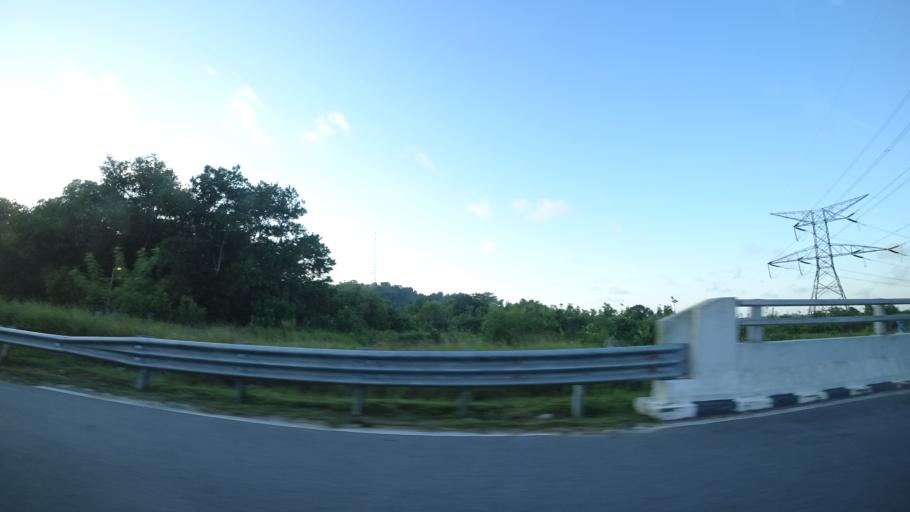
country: BN
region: Tutong
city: Tutong
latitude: 4.8230
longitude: 114.6804
